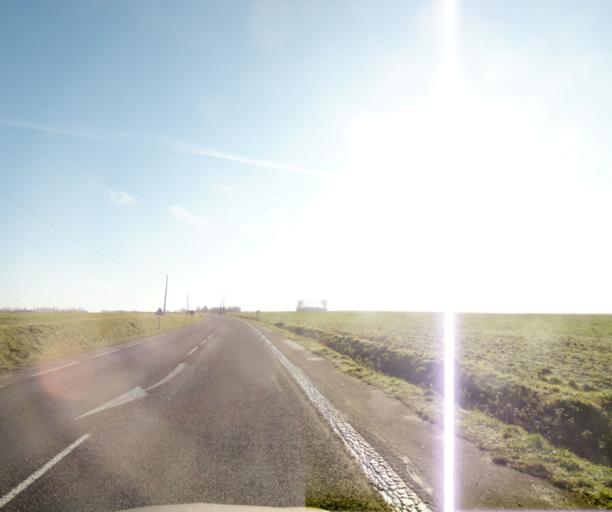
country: FR
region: Nord-Pas-de-Calais
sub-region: Departement du Nord
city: Saultain
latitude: 50.3280
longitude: 3.5599
